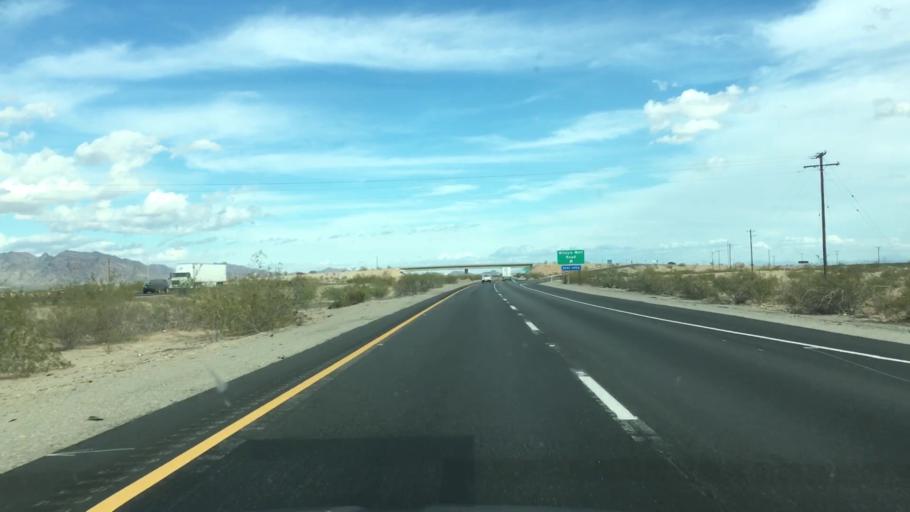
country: US
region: California
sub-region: Riverside County
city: Mesa Verde
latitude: 33.6074
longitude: -114.9072
